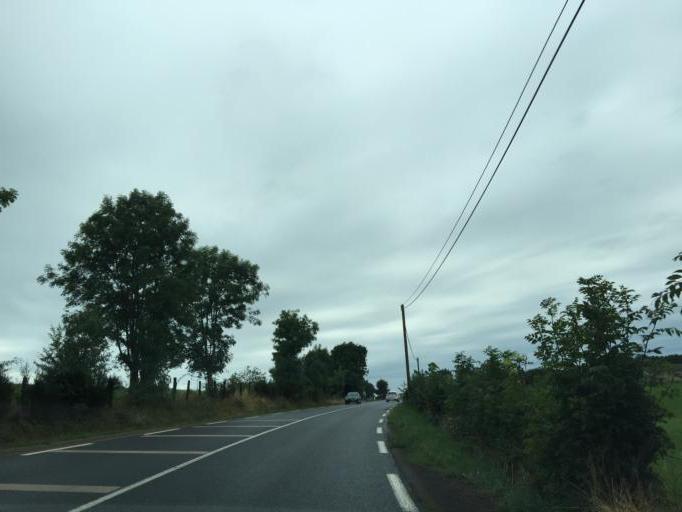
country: FR
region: Midi-Pyrenees
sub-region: Departement de l'Aveyron
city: Laguiole
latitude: 44.6093
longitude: 2.8056
